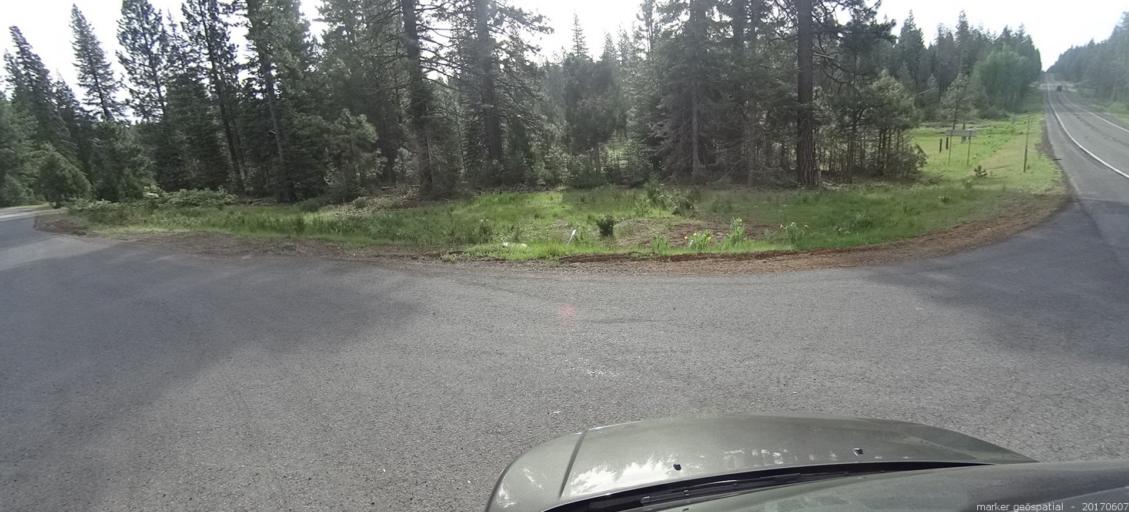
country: US
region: California
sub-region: Shasta County
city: Burney
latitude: 41.1794
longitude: -121.7090
